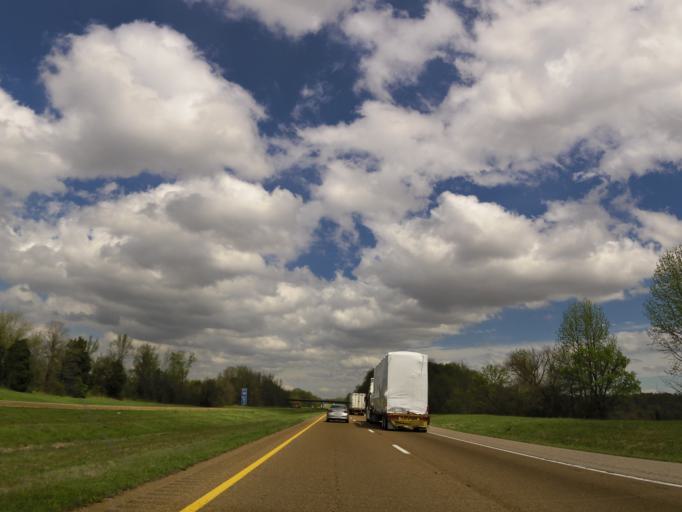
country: US
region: Tennessee
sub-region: Tipton County
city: Mason
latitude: 35.3794
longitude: -89.4441
